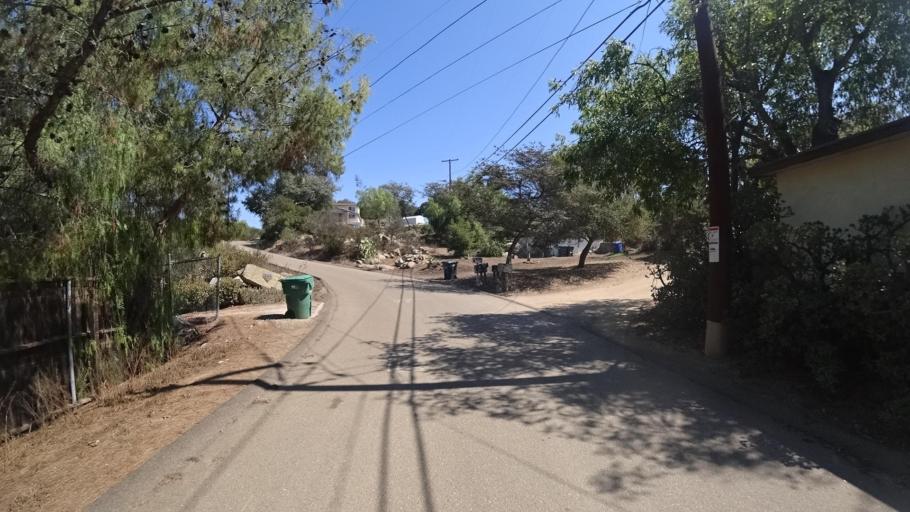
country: US
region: California
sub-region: San Diego County
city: Crest
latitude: 32.8081
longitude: -116.8631
